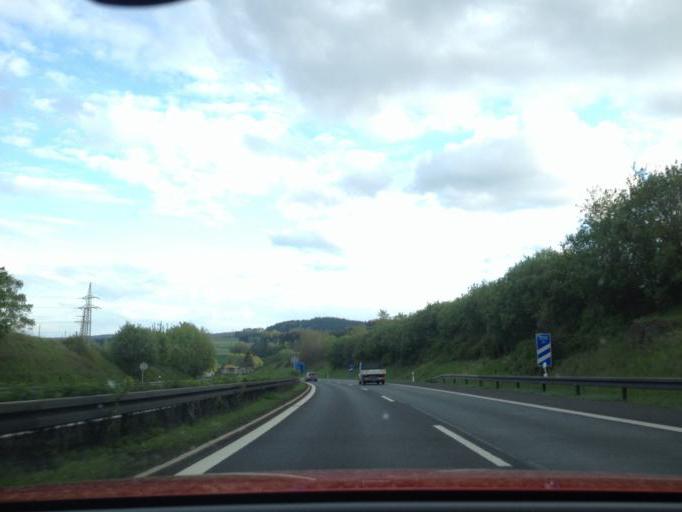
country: DE
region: Bavaria
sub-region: Upper Franconia
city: Marktredwitz
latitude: 50.0094
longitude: 12.1086
